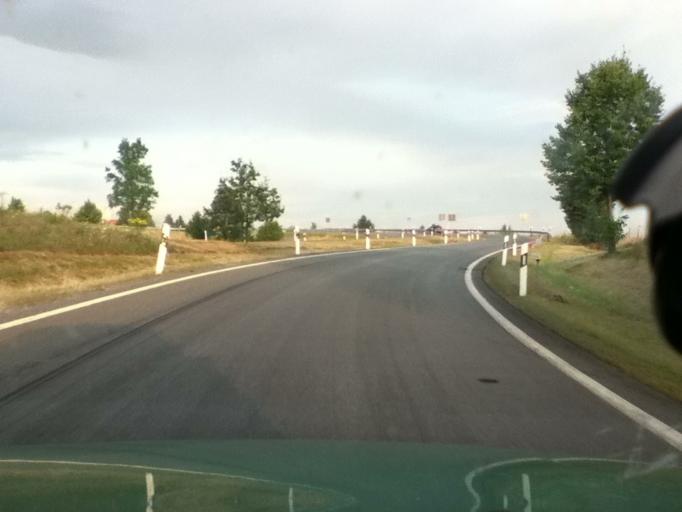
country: DE
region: Saxony
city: Weissenberg
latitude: 51.2061
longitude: 14.6616
